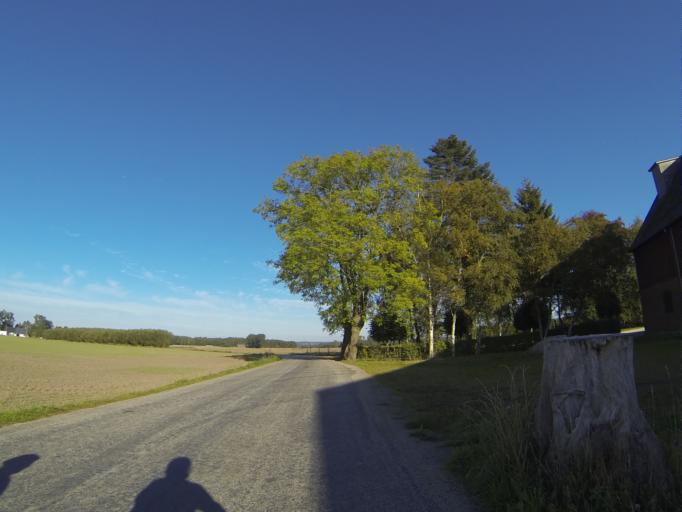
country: SE
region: Skane
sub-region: Eslovs Kommun
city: Eslov
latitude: 55.7270
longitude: 13.3543
